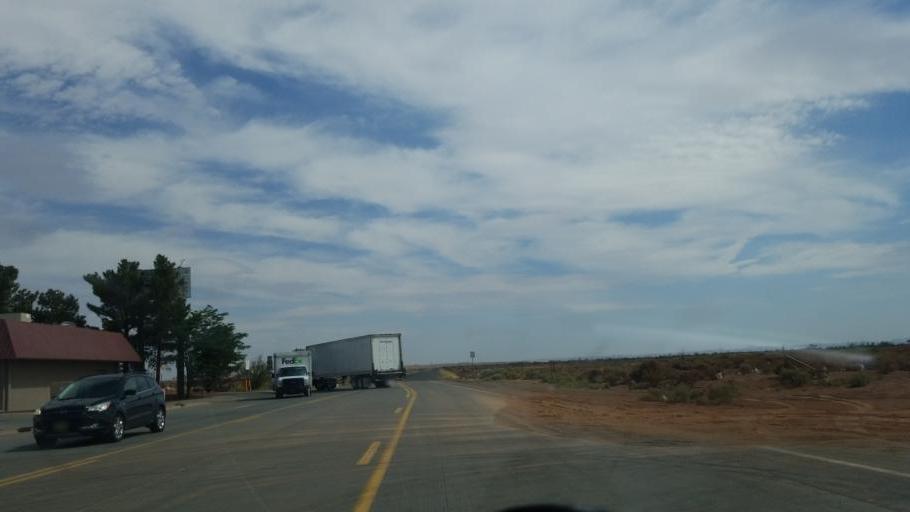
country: US
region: Arizona
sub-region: Navajo County
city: Winslow
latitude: 35.0427
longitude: -110.6980
